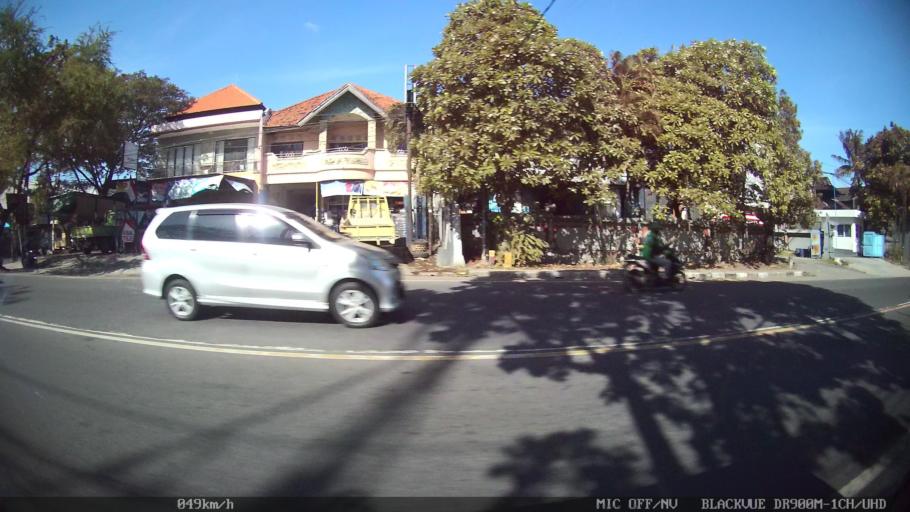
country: ID
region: Bali
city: Banjar Kertasari
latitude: -8.6330
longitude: 115.1979
